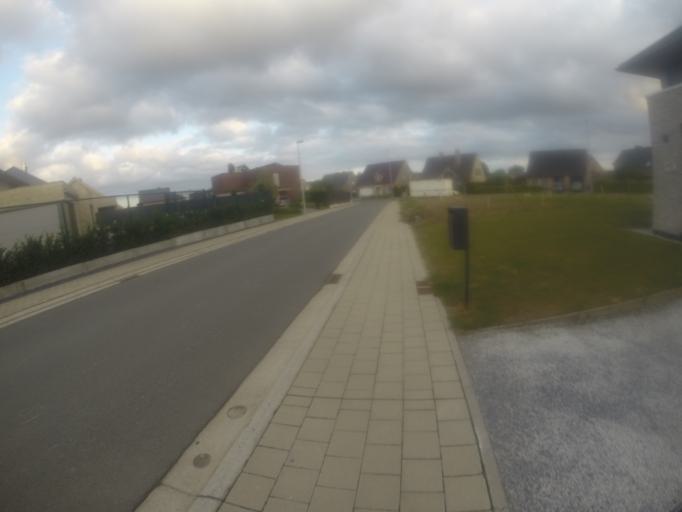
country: BE
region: Flanders
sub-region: Provincie West-Vlaanderen
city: Poperinge
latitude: 50.8535
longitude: 2.7115
